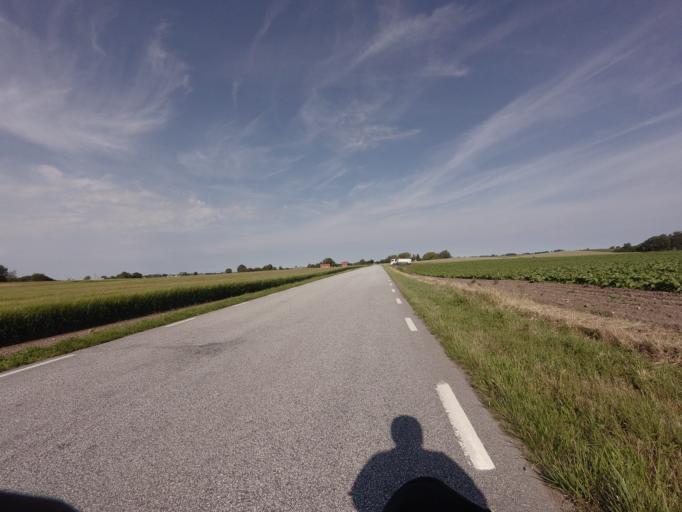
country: SE
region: Skane
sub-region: Malmo
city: Oxie
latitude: 55.4938
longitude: 13.0895
